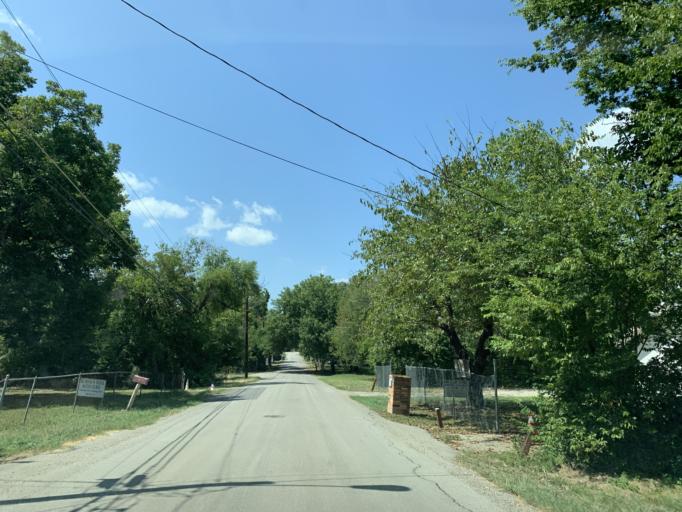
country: US
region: Texas
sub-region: Dallas County
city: Dallas
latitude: 32.7102
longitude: -96.7692
